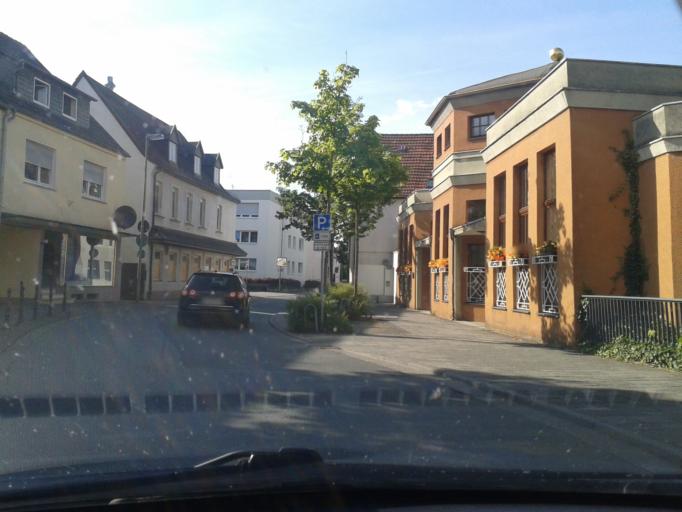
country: DE
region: North Rhine-Westphalia
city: Bad Lippspringe
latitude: 51.7806
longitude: 8.8220
